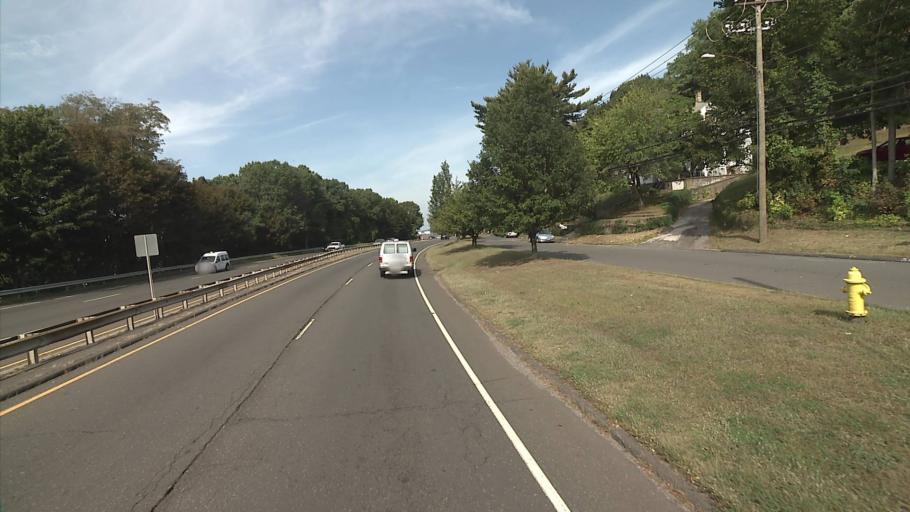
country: US
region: Connecticut
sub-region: New Haven County
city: Derby
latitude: 41.3094
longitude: -73.0745
